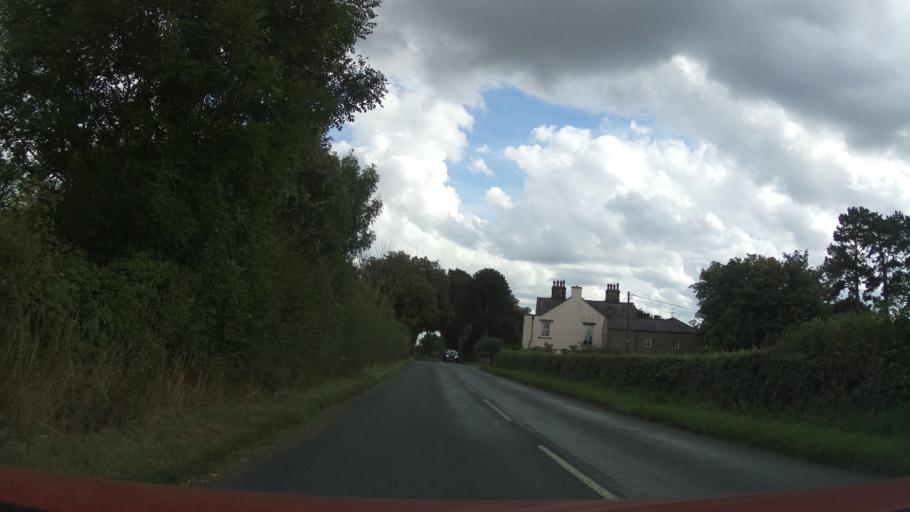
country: GB
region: England
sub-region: North Yorkshire
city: Bedale
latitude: 54.2413
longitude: -1.6853
